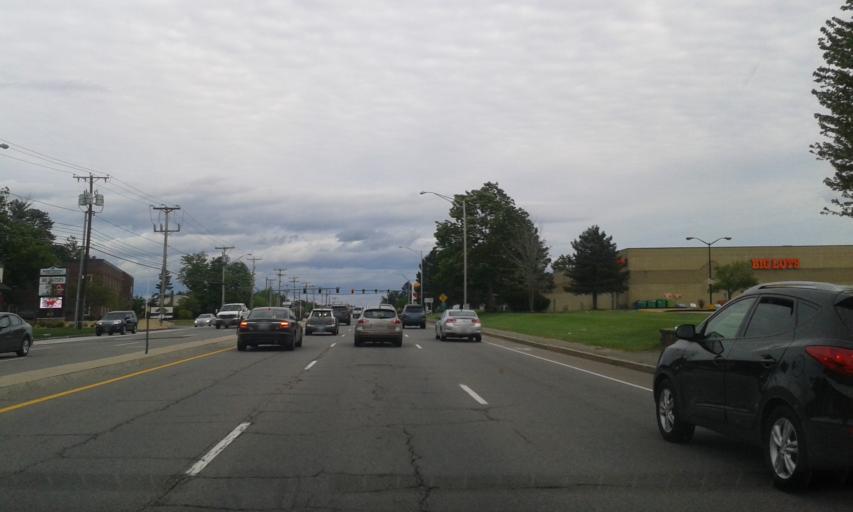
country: US
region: New Hampshire
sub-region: Hillsborough County
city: Litchfield
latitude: 42.8027
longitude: -71.5403
